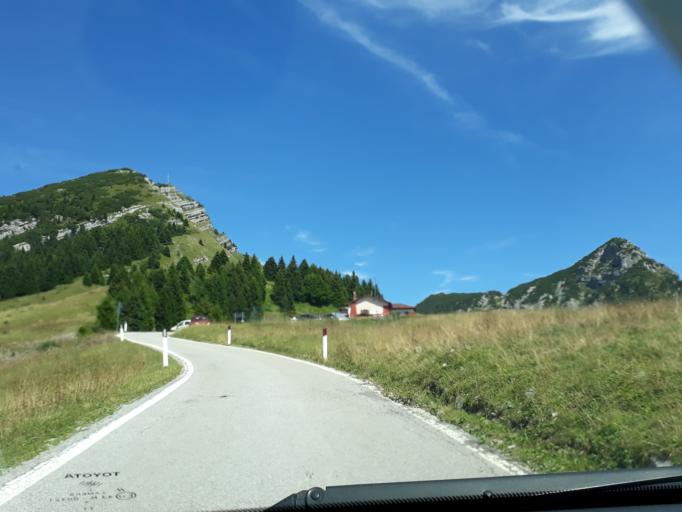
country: IT
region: Trentino-Alto Adige
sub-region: Provincia di Trento
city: Pieve di Ledro
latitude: 45.8364
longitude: 10.6886
